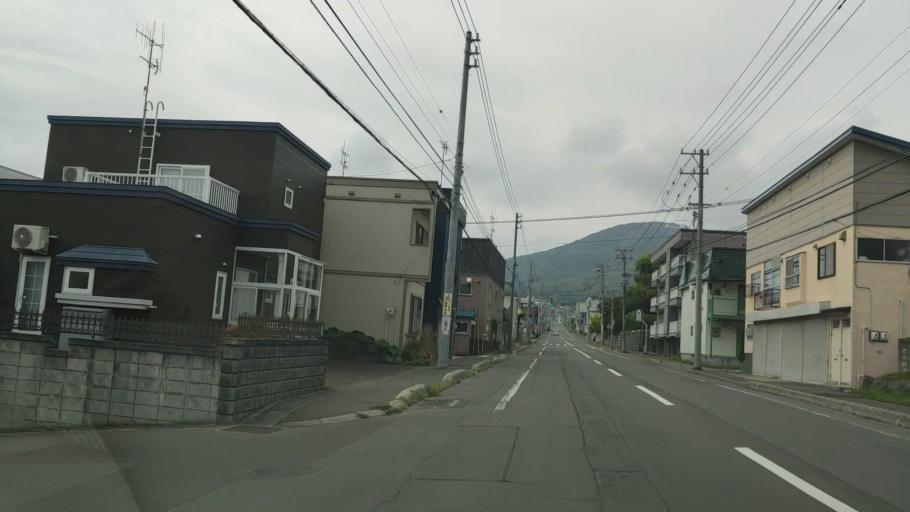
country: JP
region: Hokkaido
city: Otaru
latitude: 43.1895
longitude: 140.9869
